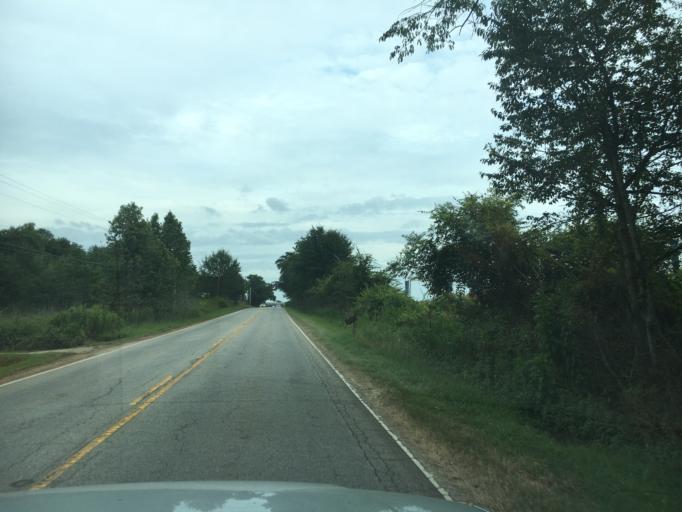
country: US
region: South Carolina
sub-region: Greenville County
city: Greer
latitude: 34.9350
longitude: -82.1998
